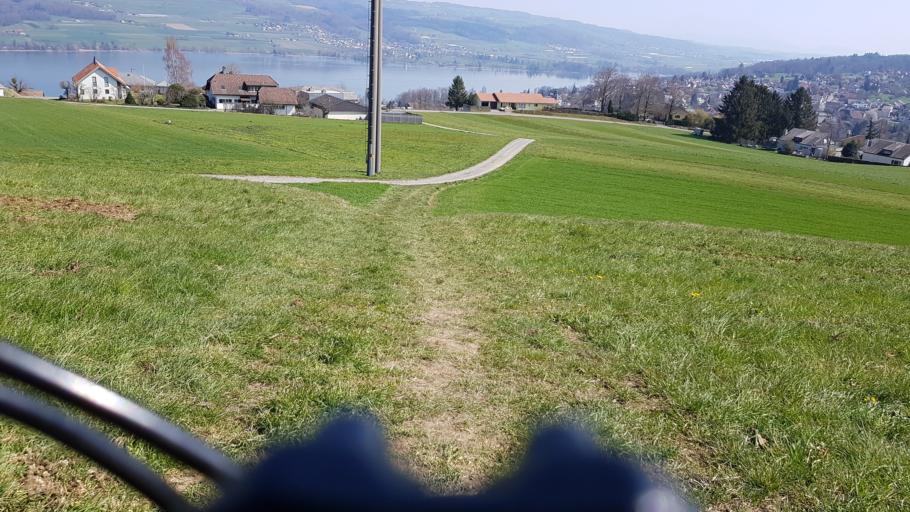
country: CH
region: Aargau
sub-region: Bezirk Kulm
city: Reinach
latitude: 47.2717
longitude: 8.1941
